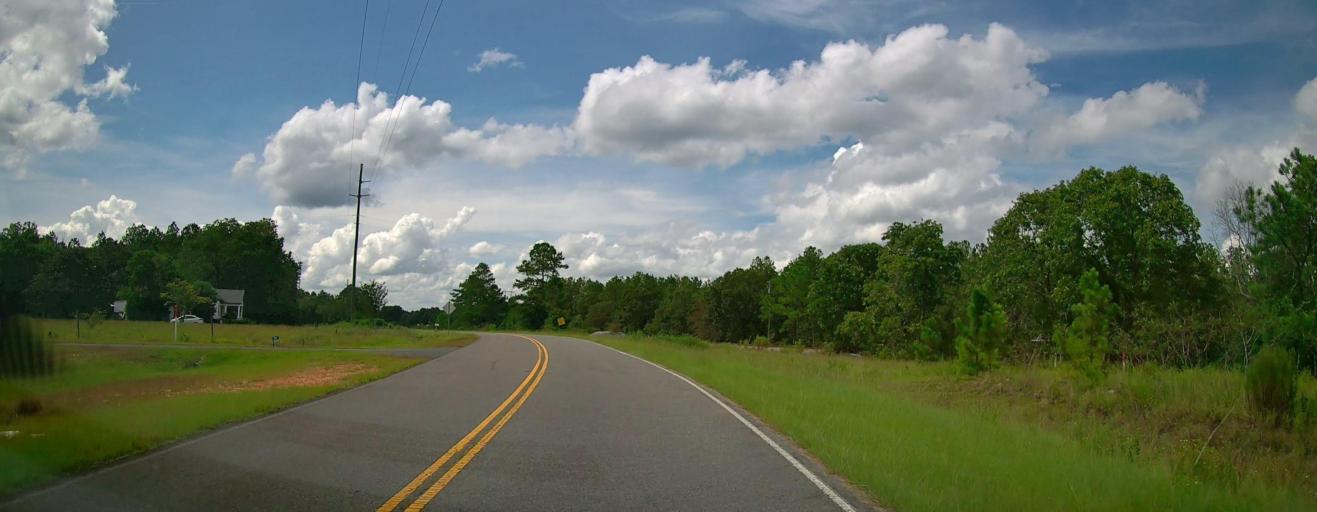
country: US
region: Georgia
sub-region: Taylor County
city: Butler
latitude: 32.5895
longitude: -84.3576
